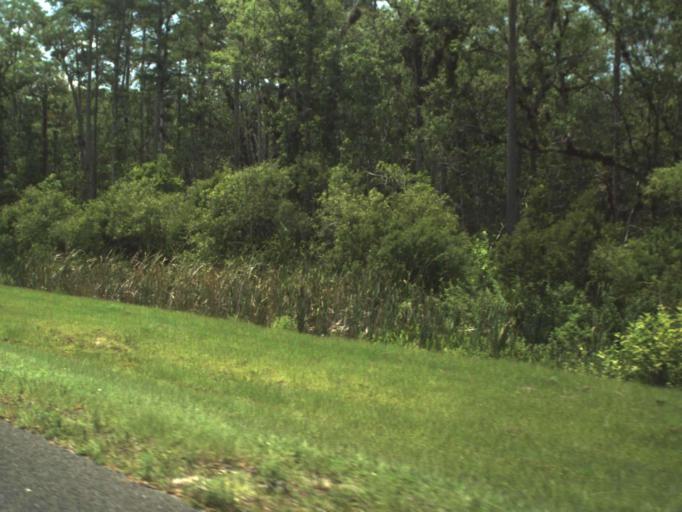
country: US
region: Florida
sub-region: Volusia County
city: Lake Helen
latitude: 29.0262
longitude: -81.1925
